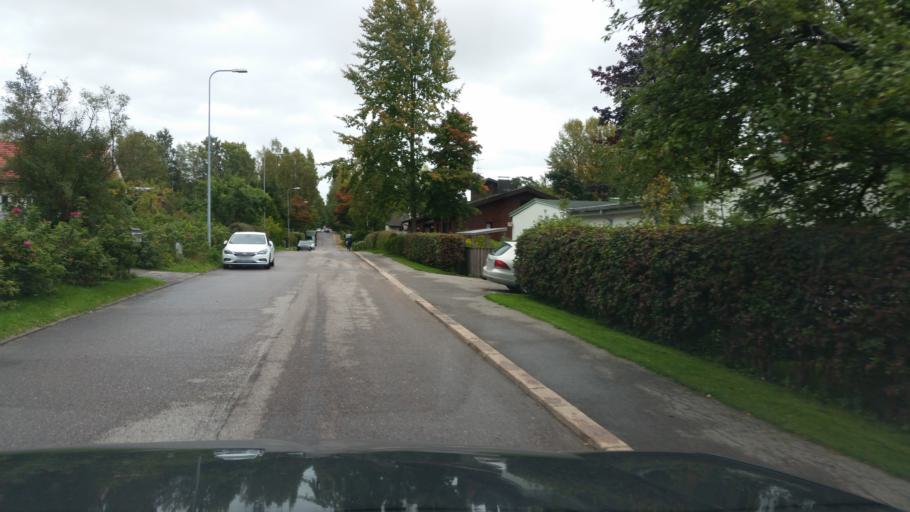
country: FI
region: Uusimaa
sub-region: Helsinki
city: Helsinki
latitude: 60.2442
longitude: 24.9278
